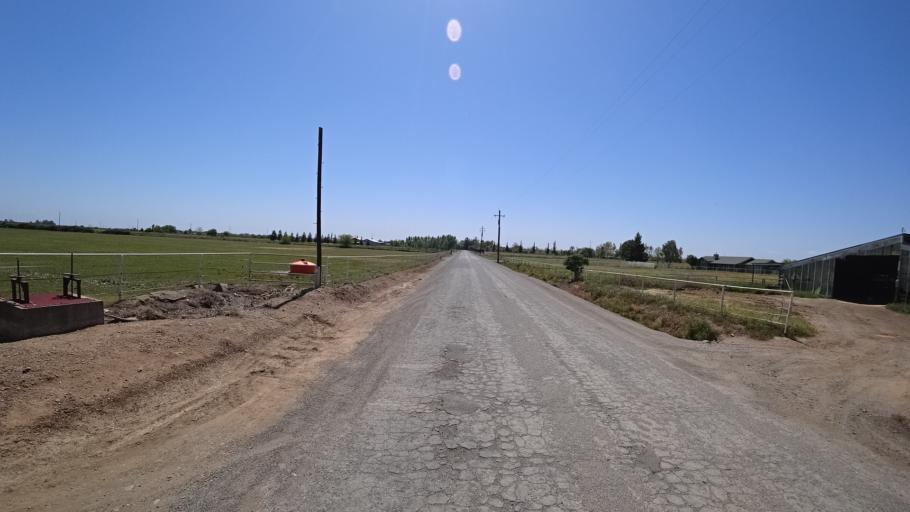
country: US
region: California
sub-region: Glenn County
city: Orland
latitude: 39.7738
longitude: -122.1503
